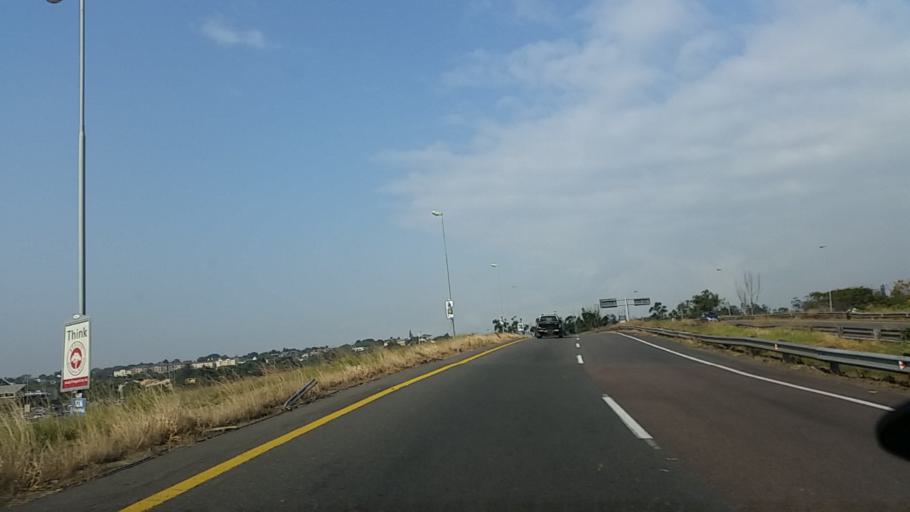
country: ZA
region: KwaZulu-Natal
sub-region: eThekwini Metropolitan Municipality
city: Berea
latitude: -29.8292
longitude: 30.9586
